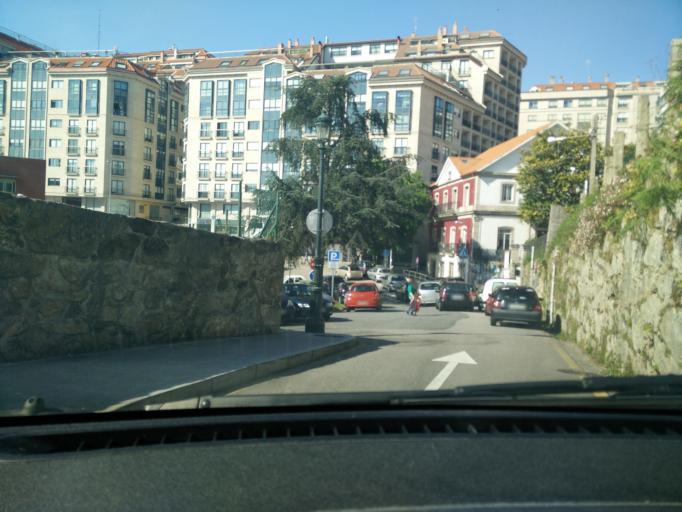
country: ES
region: Galicia
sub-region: Provincia de Pontevedra
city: Vigo
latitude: 42.2256
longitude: -8.7276
